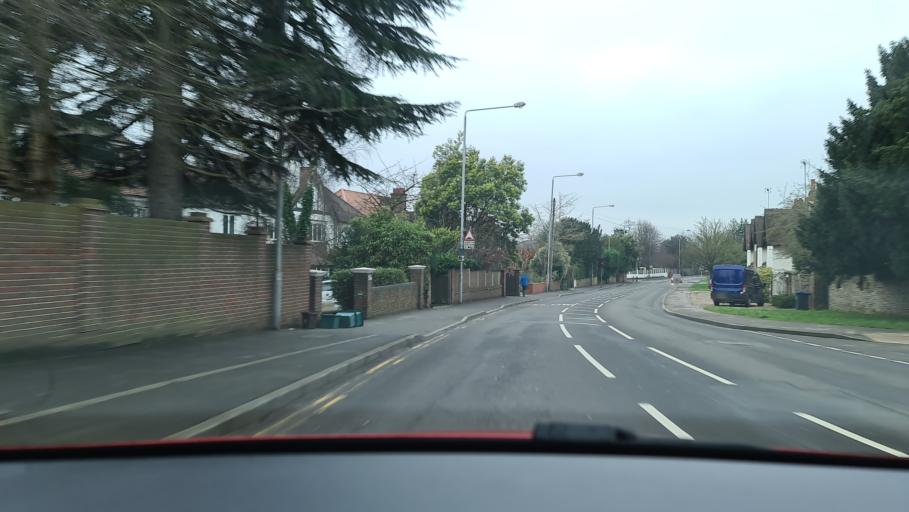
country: GB
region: England
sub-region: Greater London
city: New Malden
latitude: 51.4143
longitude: -0.2689
